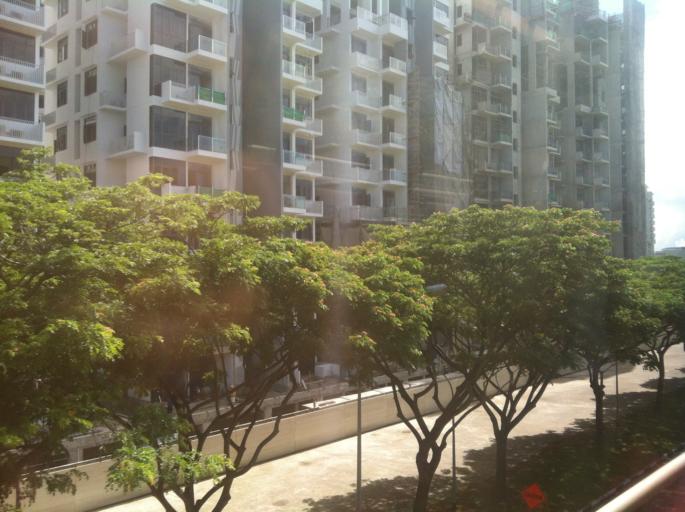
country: SG
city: Singapore
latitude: 1.3264
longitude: 103.9441
